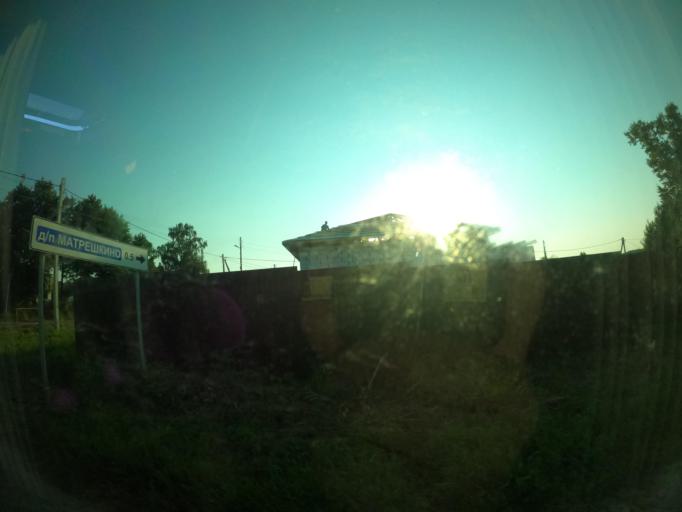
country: RU
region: Moskovskaya
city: Serpukhov
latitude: 54.9549
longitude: 37.3378
